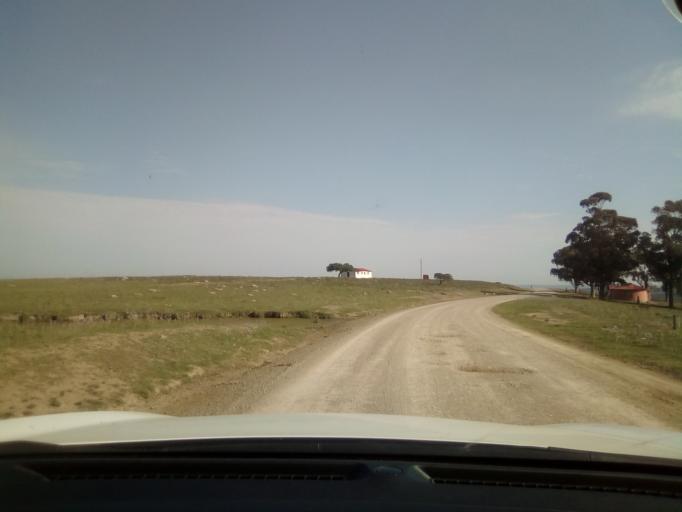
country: ZA
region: Eastern Cape
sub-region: Buffalo City Metropolitan Municipality
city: Bhisho
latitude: -32.9870
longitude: 27.2566
